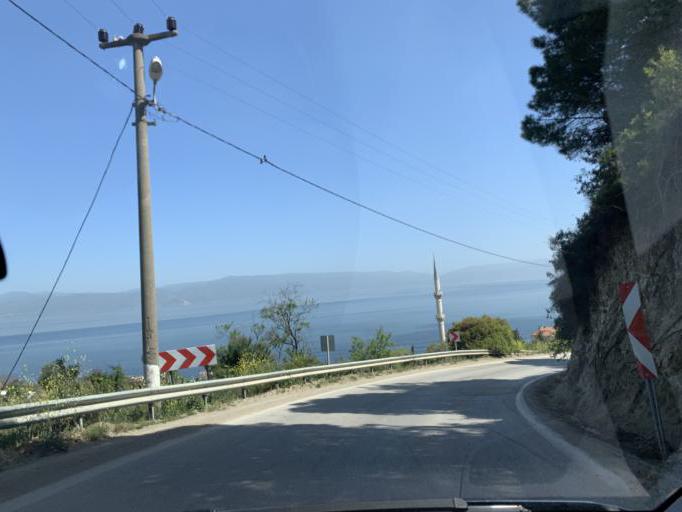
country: TR
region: Bursa
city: Niluefer
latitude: 40.3541
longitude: 28.9697
